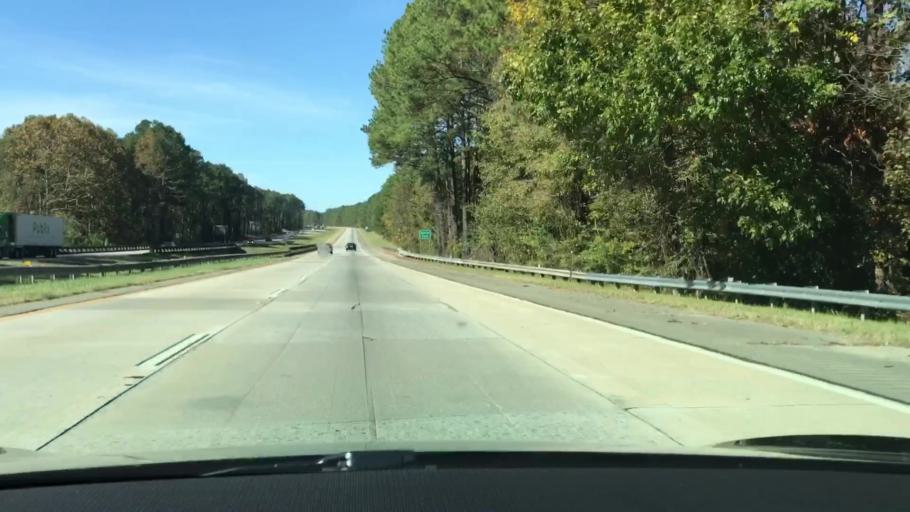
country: US
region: Georgia
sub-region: Taliaferro County
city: Crawfordville
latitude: 33.5303
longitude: -82.9183
